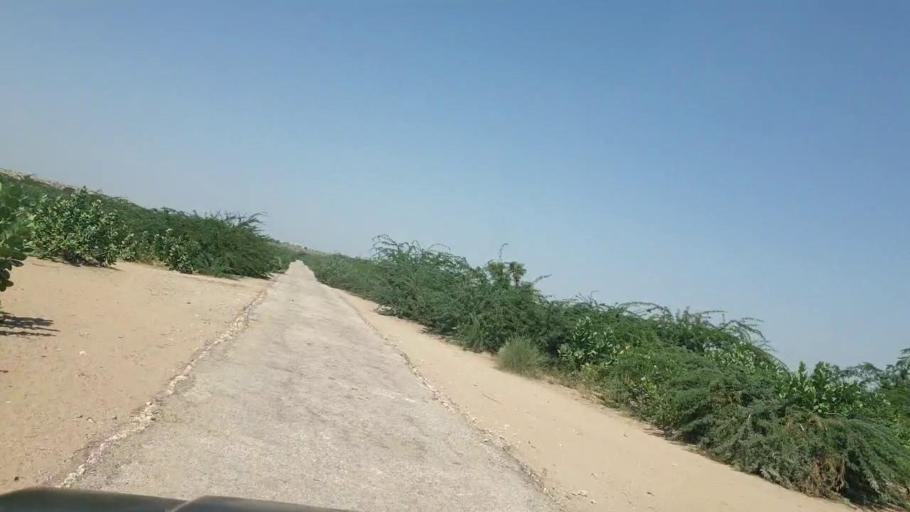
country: PK
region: Sindh
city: Chor
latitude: 25.4033
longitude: 70.3098
